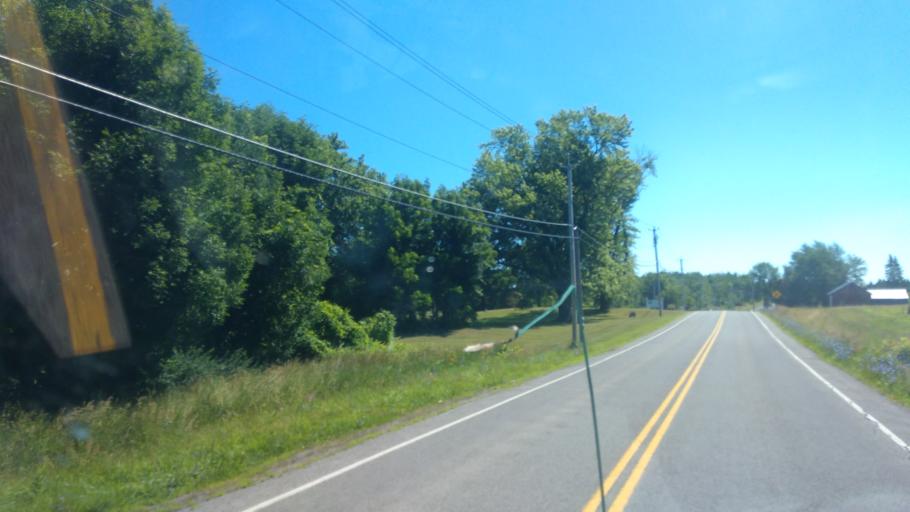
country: US
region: New York
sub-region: Wayne County
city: Williamson
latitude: 43.2836
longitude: -77.1462
